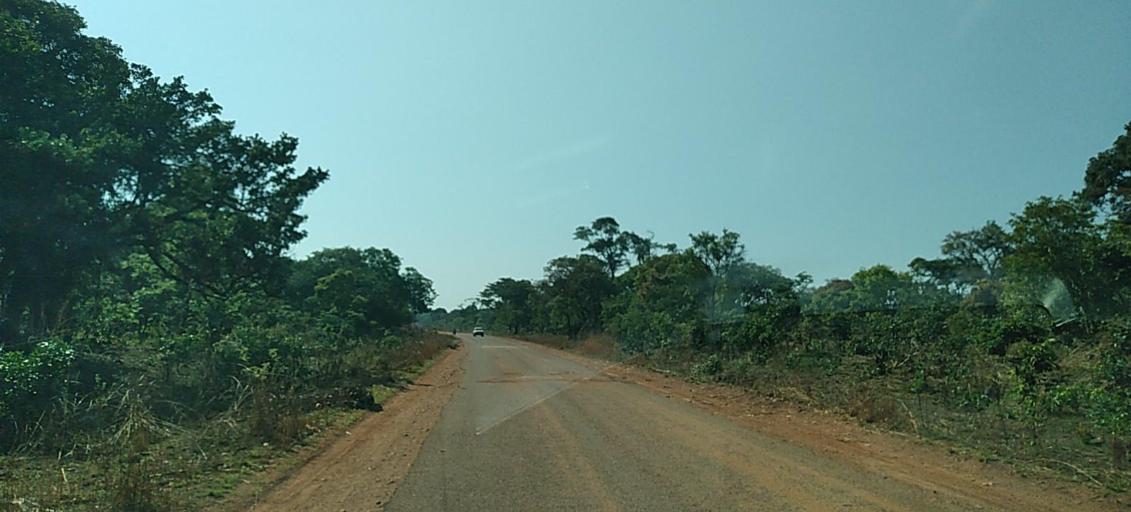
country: ZM
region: North-Western
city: Mwinilunga
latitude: -11.8998
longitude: 25.2771
